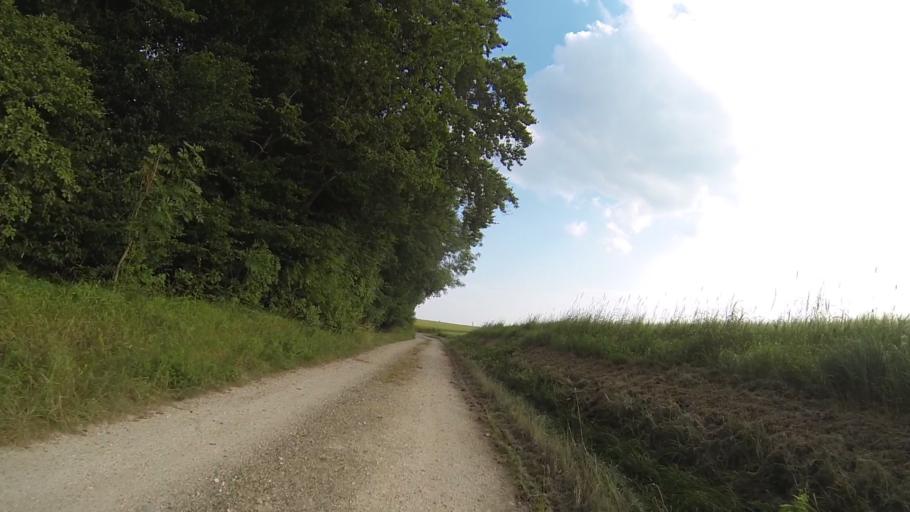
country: DE
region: Baden-Wuerttemberg
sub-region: Tuebingen Region
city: Blaubeuren
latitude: 48.4404
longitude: 9.8618
